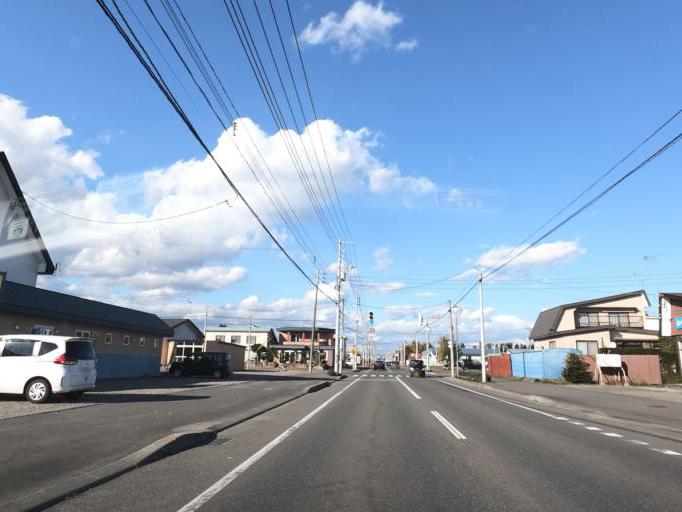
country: JP
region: Hokkaido
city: Otofuke
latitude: 43.2371
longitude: 143.2978
